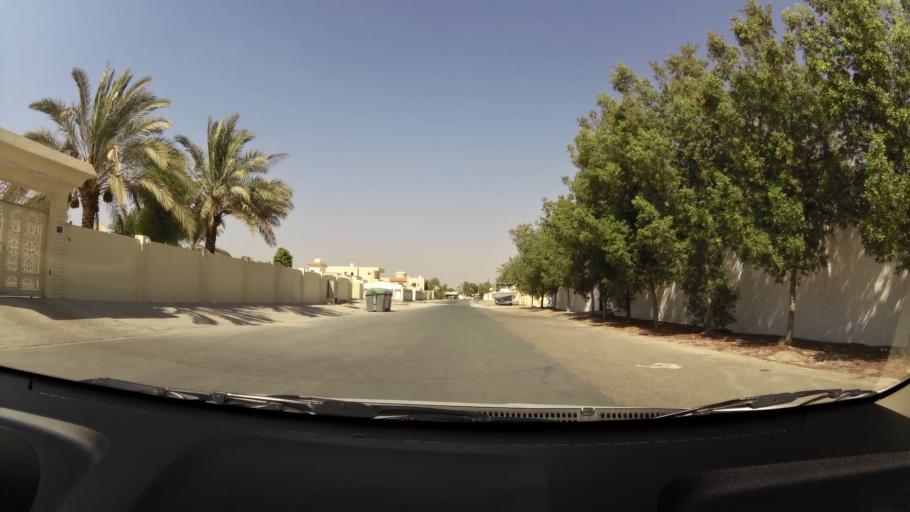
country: AE
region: Ajman
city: Ajman
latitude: 25.4176
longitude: 55.4691
